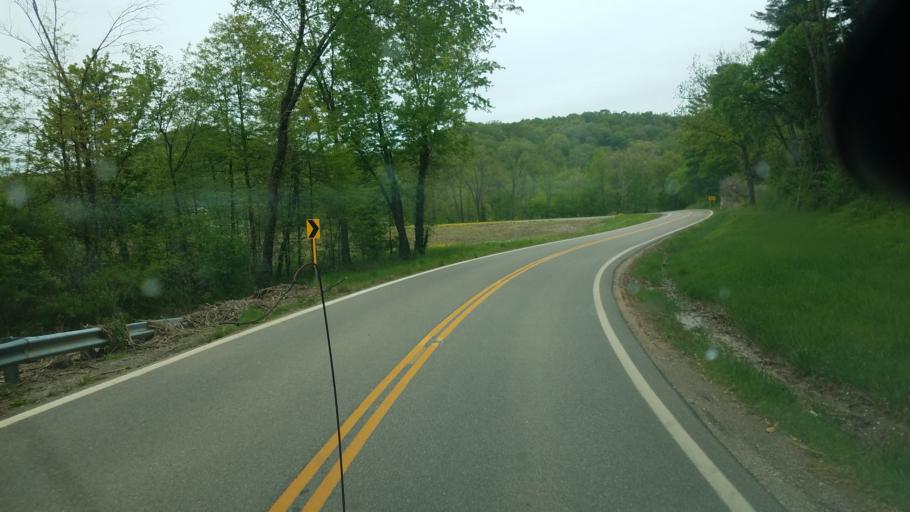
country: US
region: Ohio
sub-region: Guernsey County
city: Mantua
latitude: 40.1598
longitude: -81.6224
